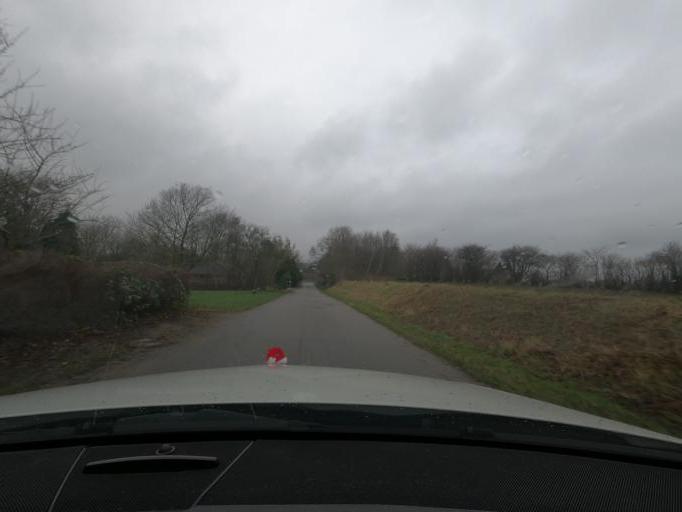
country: DK
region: South Denmark
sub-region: Haderslev Kommune
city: Starup
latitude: 55.2451
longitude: 9.6864
